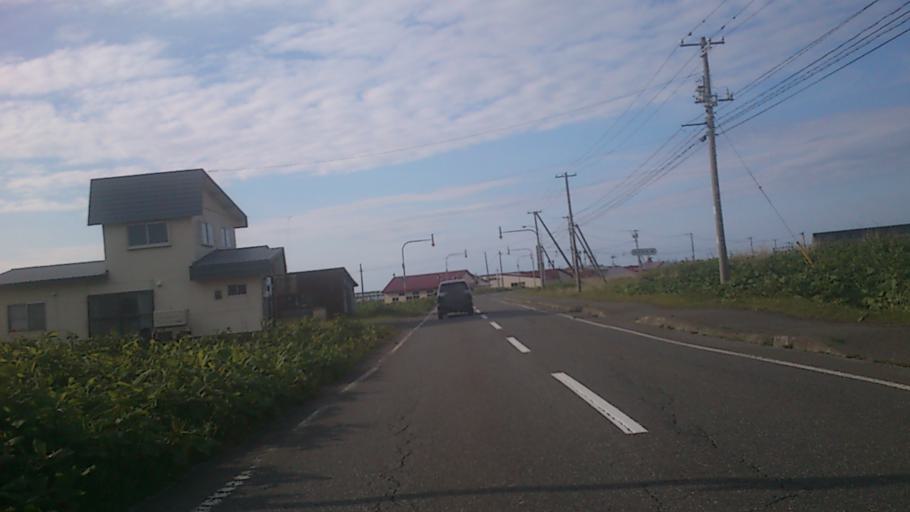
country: JP
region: Hokkaido
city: Wakkanai
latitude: 45.4230
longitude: 141.6368
